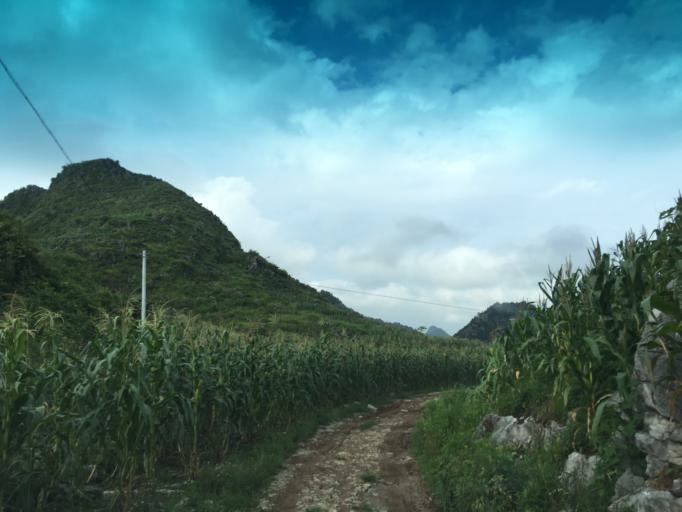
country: CN
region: Guangxi Zhuangzu Zizhiqu
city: Xinzhou
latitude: 24.9920
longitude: 105.6337
